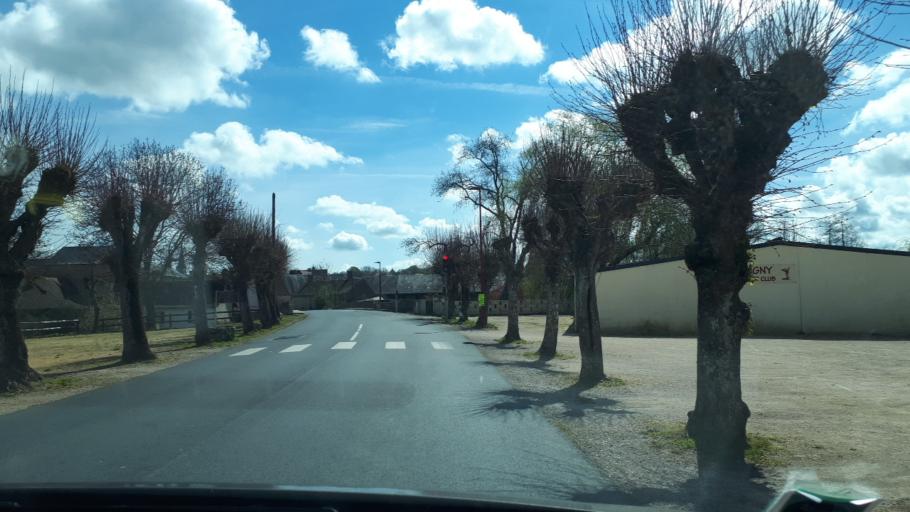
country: FR
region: Centre
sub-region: Departement du Loir-et-Cher
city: Savigny-sur-Braye
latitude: 47.8805
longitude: 0.8028
